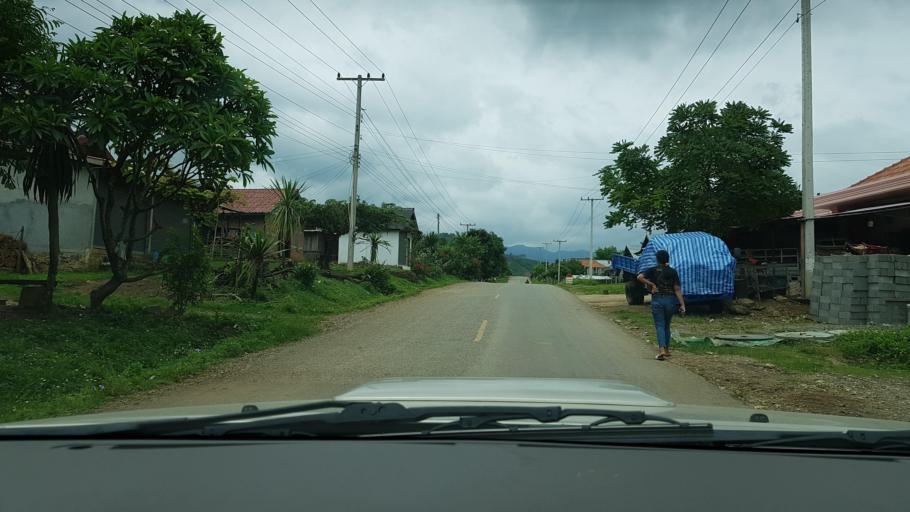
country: TH
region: Nan
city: Chaloem Phra Kiat
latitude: 19.9880
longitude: 101.2769
